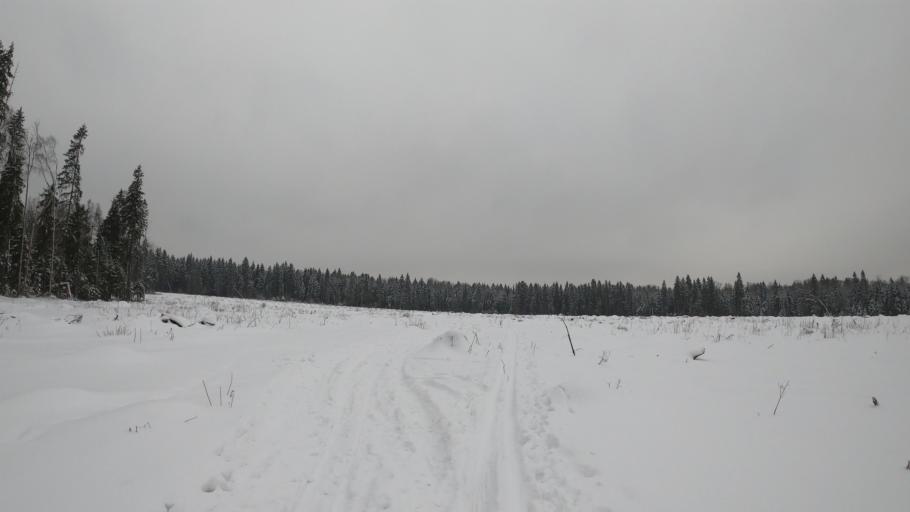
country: RU
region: Moskovskaya
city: Firsanovka
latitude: 55.9630
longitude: 37.2211
